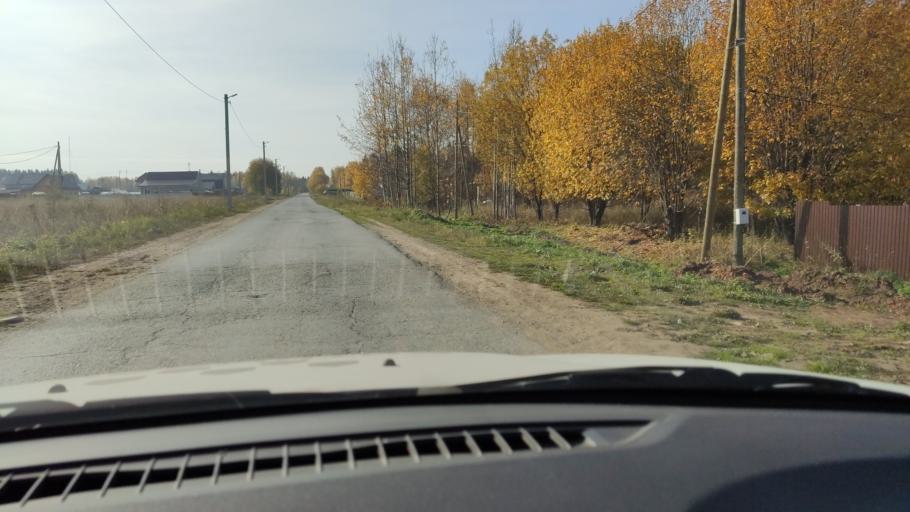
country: RU
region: Perm
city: Sylva
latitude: 58.0392
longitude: 56.7450
